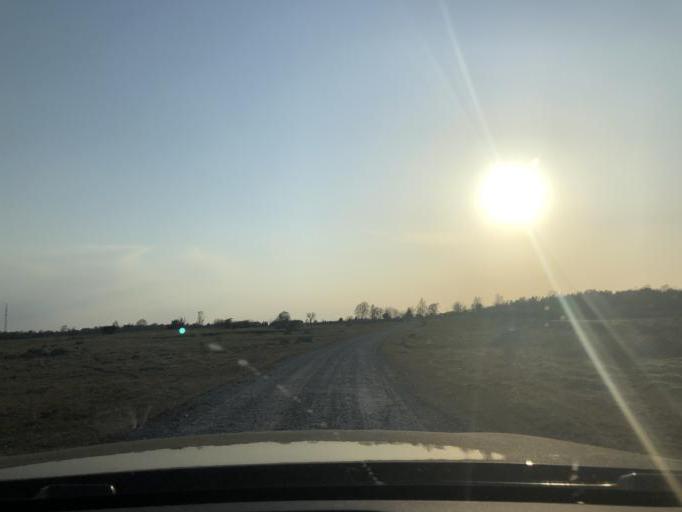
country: SE
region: Kalmar
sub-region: Morbylanga Kommun
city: Sodra Sandby
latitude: 56.5583
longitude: 16.6265
